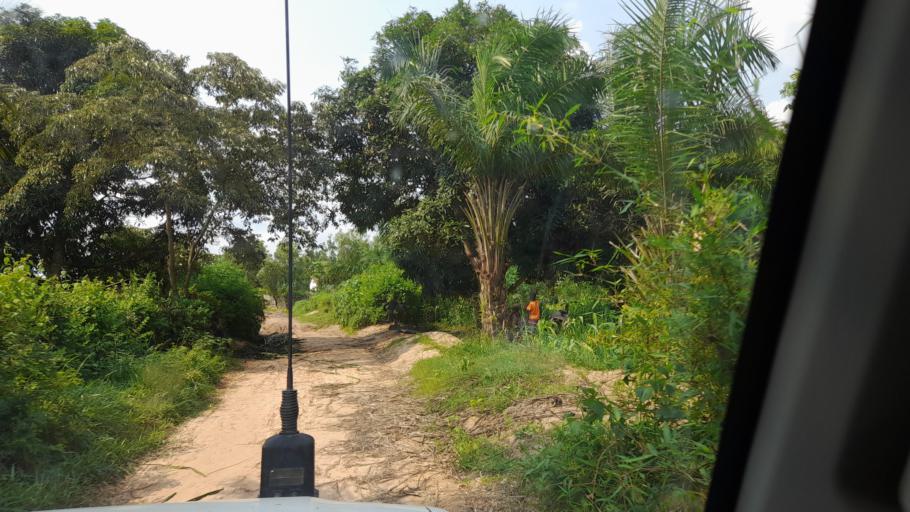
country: CD
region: Kasai-Occidental
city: Kananga
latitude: -5.9081
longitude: 22.4757
